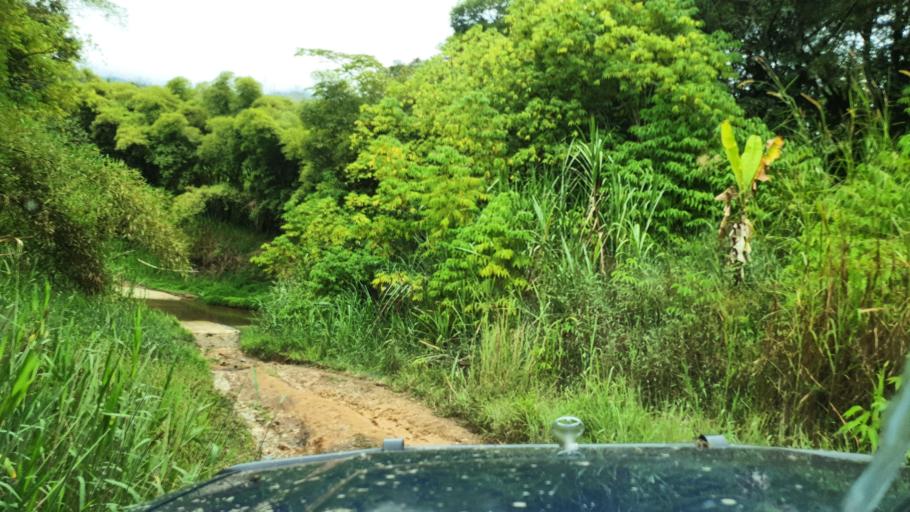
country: PG
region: Jiwaka
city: Minj
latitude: -5.9310
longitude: 144.7490
